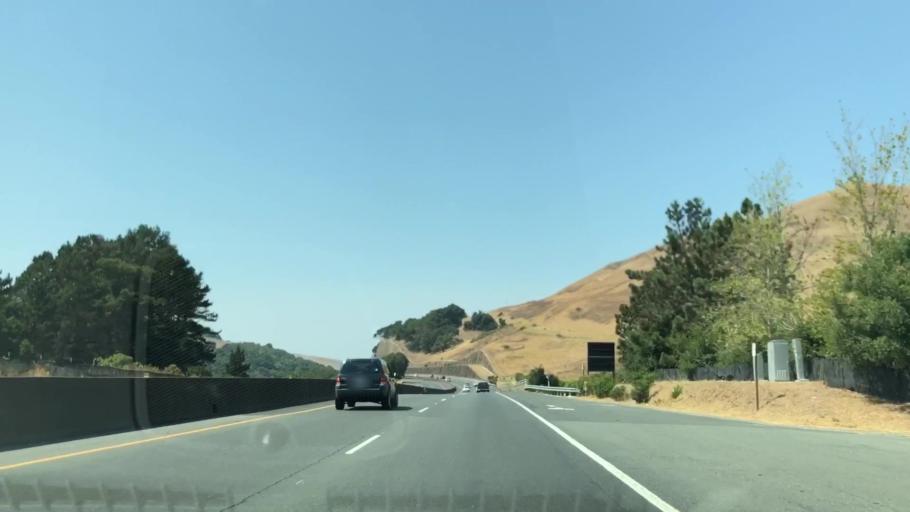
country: US
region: California
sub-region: Solano County
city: Green Valley
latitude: 38.2077
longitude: -122.1656
